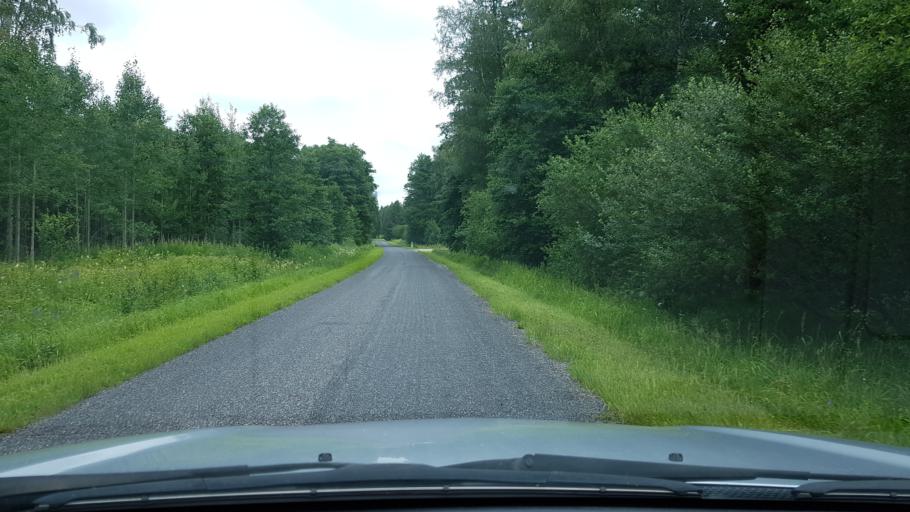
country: EE
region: Ida-Virumaa
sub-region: Narva-Joesuu linn
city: Narva-Joesuu
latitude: 59.3537
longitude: 28.0374
